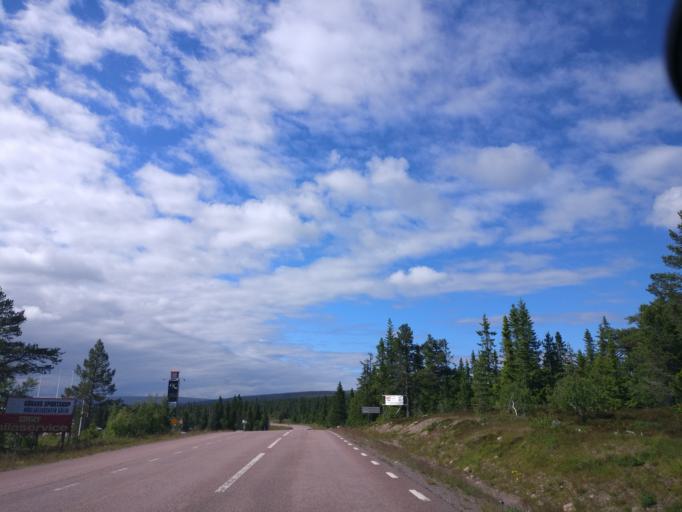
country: SE
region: Dalarna
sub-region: Malung-Saelens kommun
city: Malung
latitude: 61.1597
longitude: 13.1120
